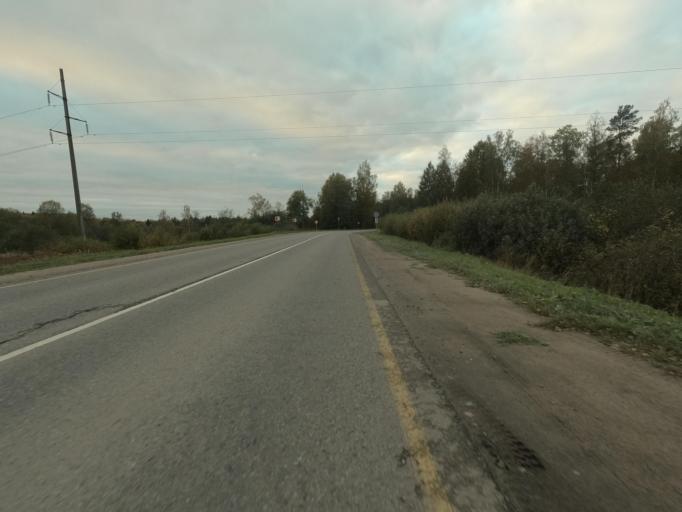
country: RU
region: Leningrad
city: Pavlovo
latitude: 59.8023
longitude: 30.9379
